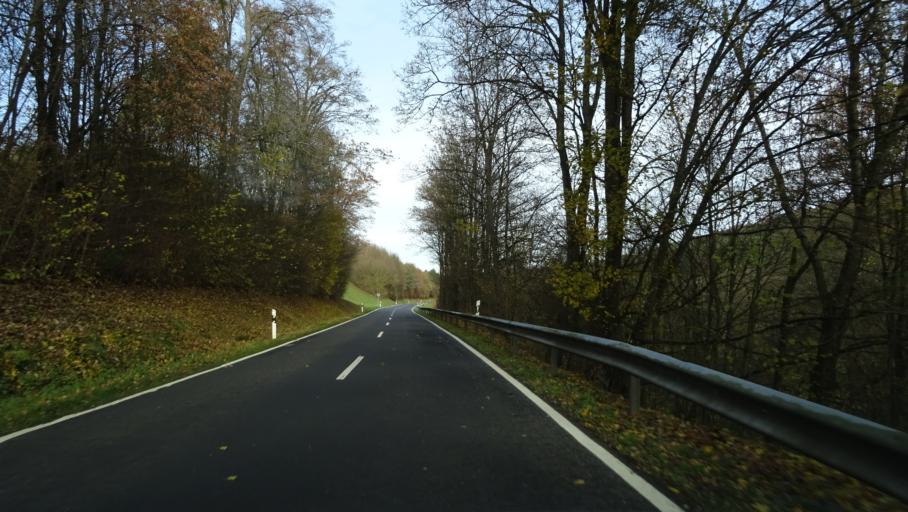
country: DE
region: Baden-Wuerttemberg
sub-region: Karlsruhe Region
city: Mosbach
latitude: 49.3619
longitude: 9.1271
